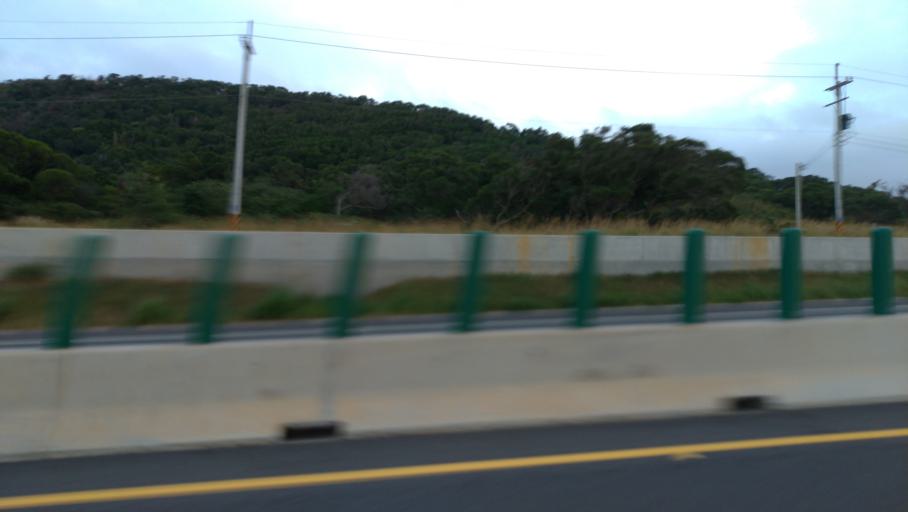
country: TW
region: Taiwan
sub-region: Miaoli
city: Miaoli
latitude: 24.5340
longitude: 120.6975
